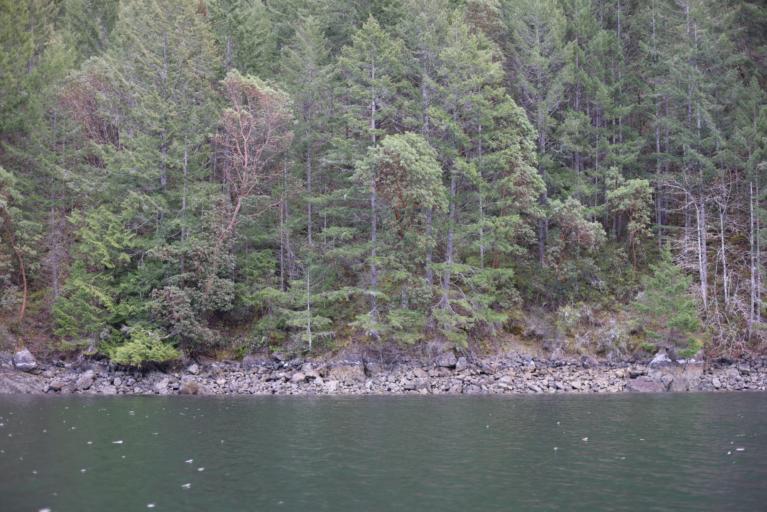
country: CA
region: British Columbia
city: Langford
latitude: 48.5044
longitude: -123.5439
